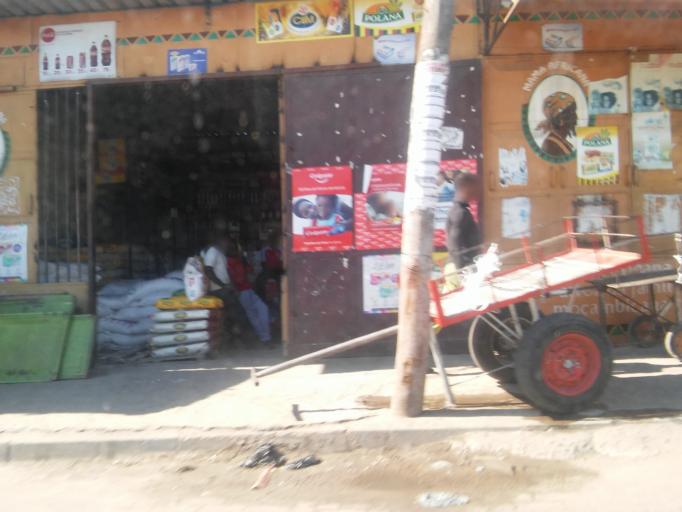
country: MZ
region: Maputo City
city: Maputo
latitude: -25.8309
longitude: 32.5754
